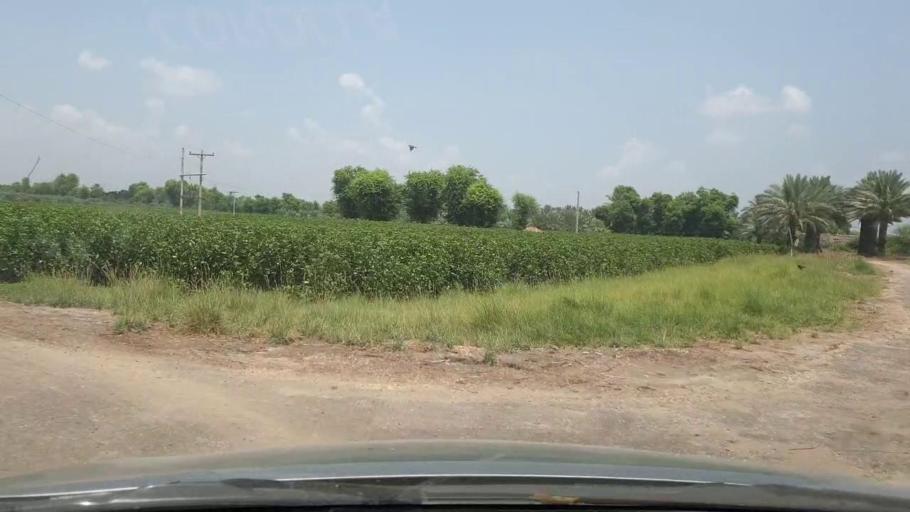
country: PK
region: Sindh
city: Khairpur
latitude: 27.4726
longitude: 68.7328
